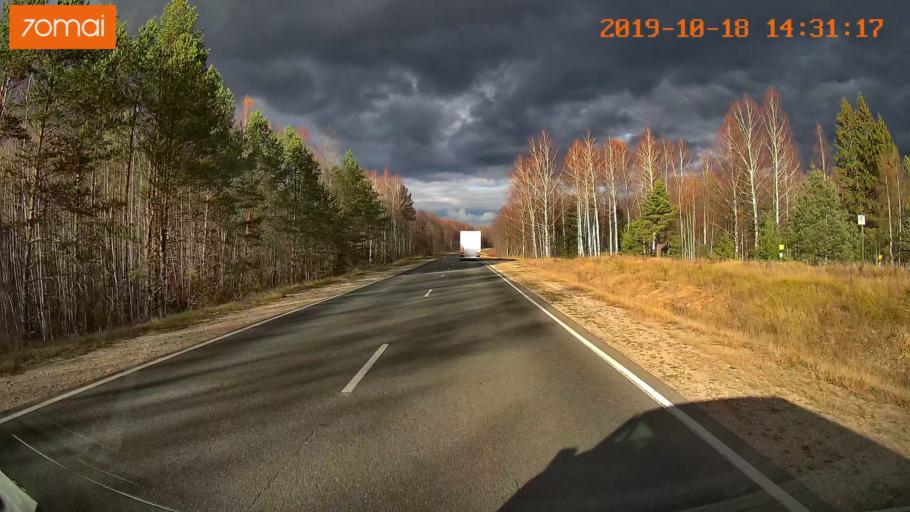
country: RU
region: Rjazan
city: Tuma
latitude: 55.1807
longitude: 40.5693
